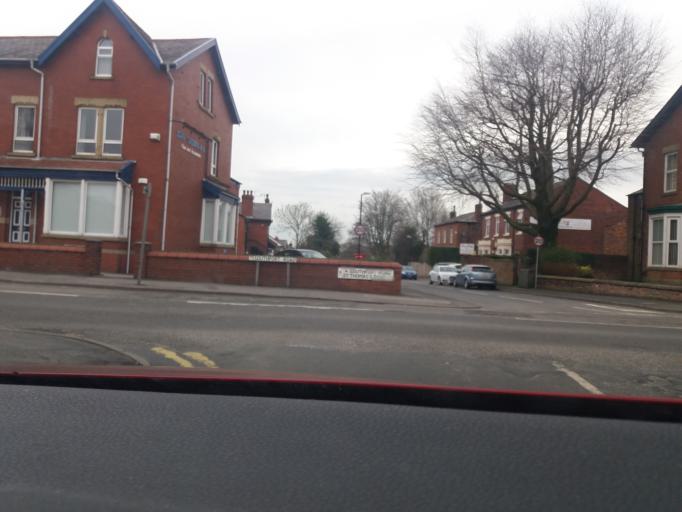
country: GB
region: England
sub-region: Lancashire
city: Chorley
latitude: 53.6533
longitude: -2.6375
